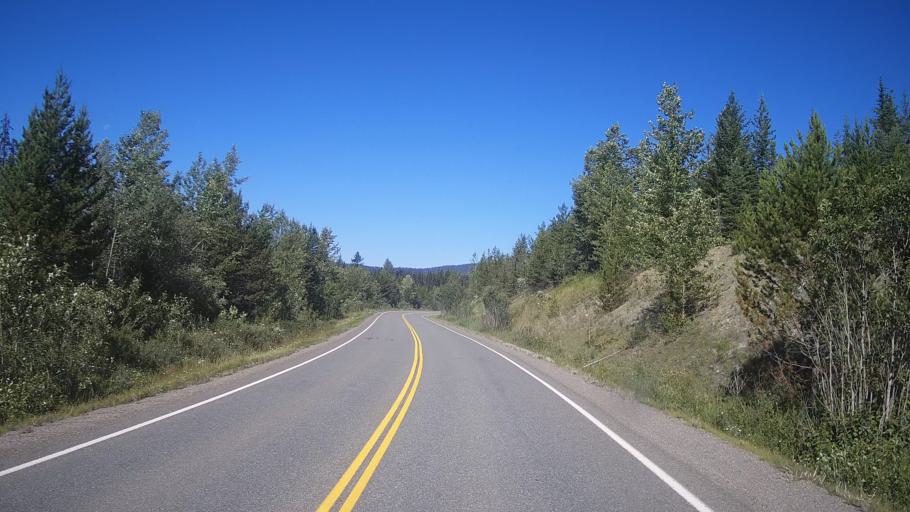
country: CA
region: British Columbia
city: Kamloops
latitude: 51.4955
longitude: -120.4124
